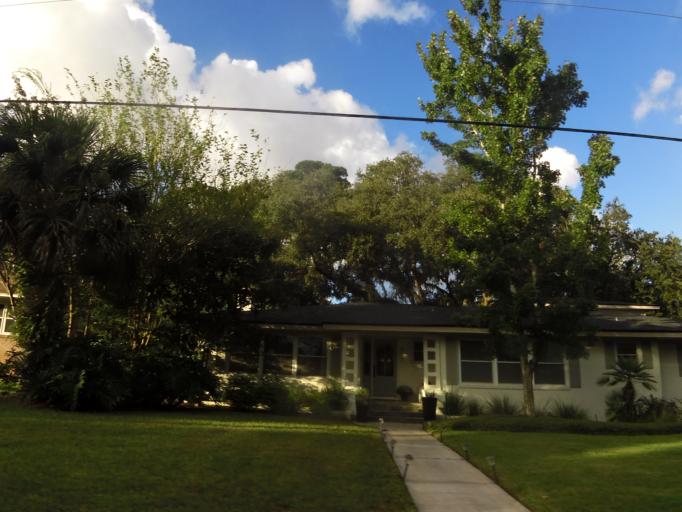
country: US
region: Florida
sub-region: Duval County
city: Jacksonville
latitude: 30.2882
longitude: -81.6561
